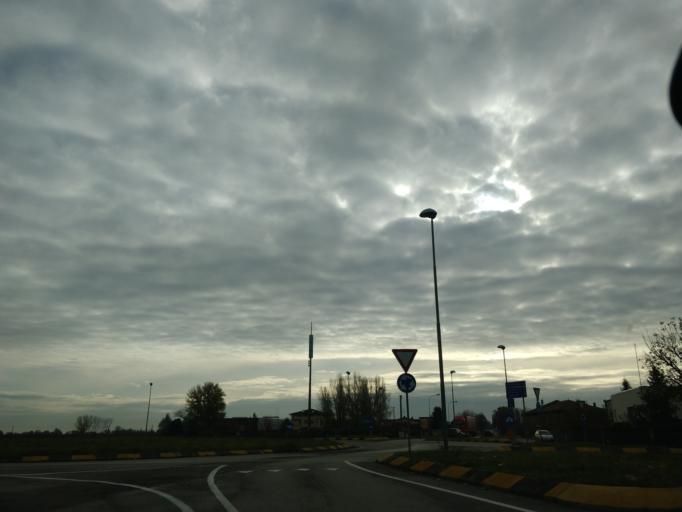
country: IT
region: Emilia-Romagna
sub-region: Provincia di Bologna
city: Castello d'Argile
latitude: 44.6763
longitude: 11.2982
